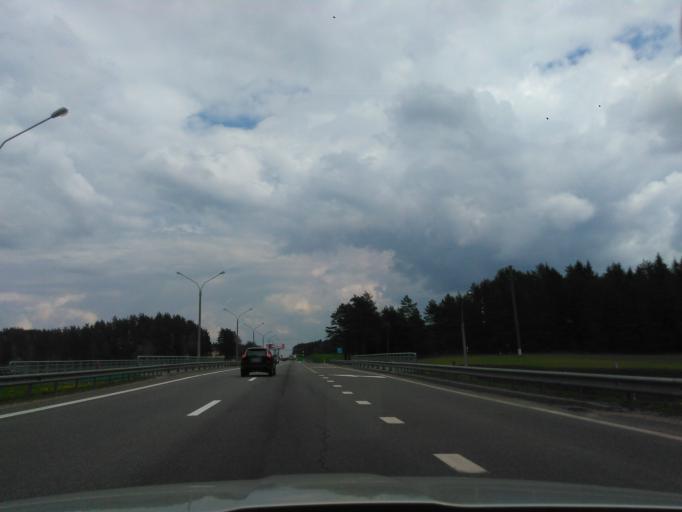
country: BY
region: Minsk
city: Korolev Stan
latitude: 53.9767
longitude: 27.7682
